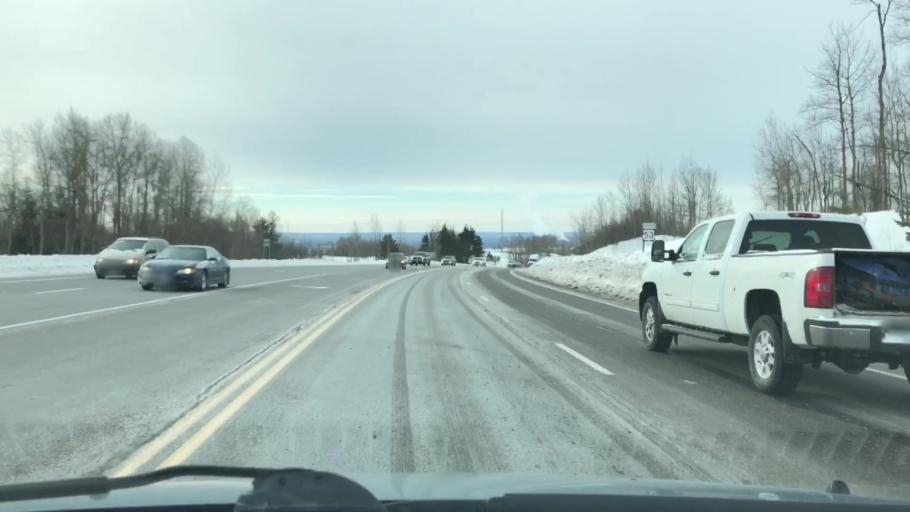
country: US
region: Minnesota
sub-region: Saint Louis County
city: Duluth
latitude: 46.7821
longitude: -92.1387
